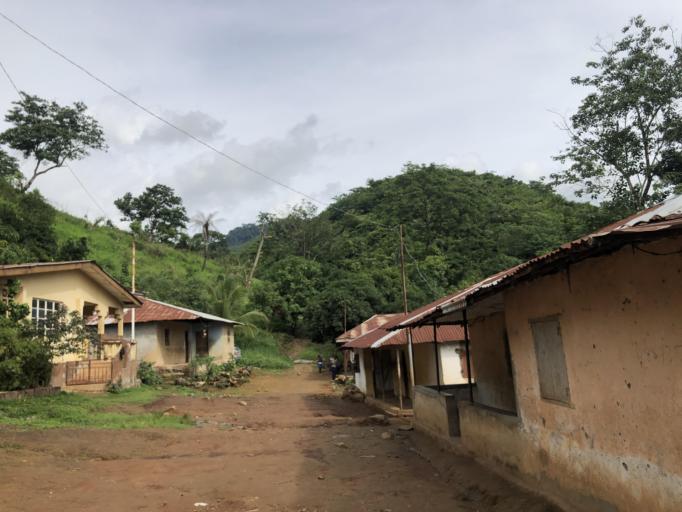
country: SL
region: Northern Province
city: Bumbuna
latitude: 9.0411
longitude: -11.7405
